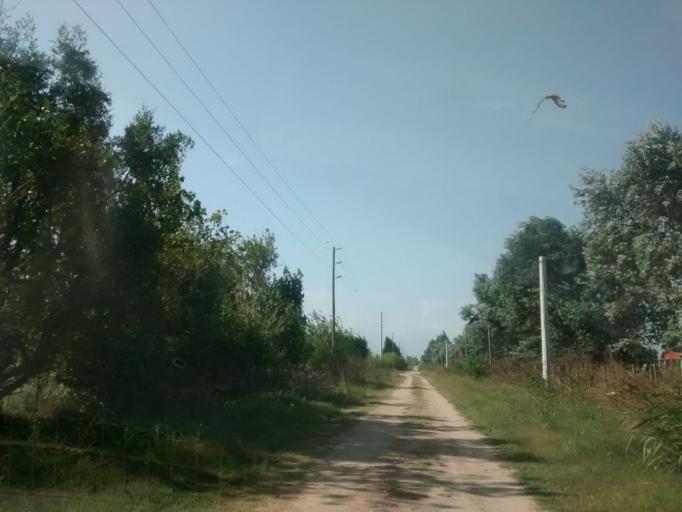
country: AR
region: Buenos Aires
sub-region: Partido de La Plata
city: La Plata
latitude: -35.0092
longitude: -57.9061
